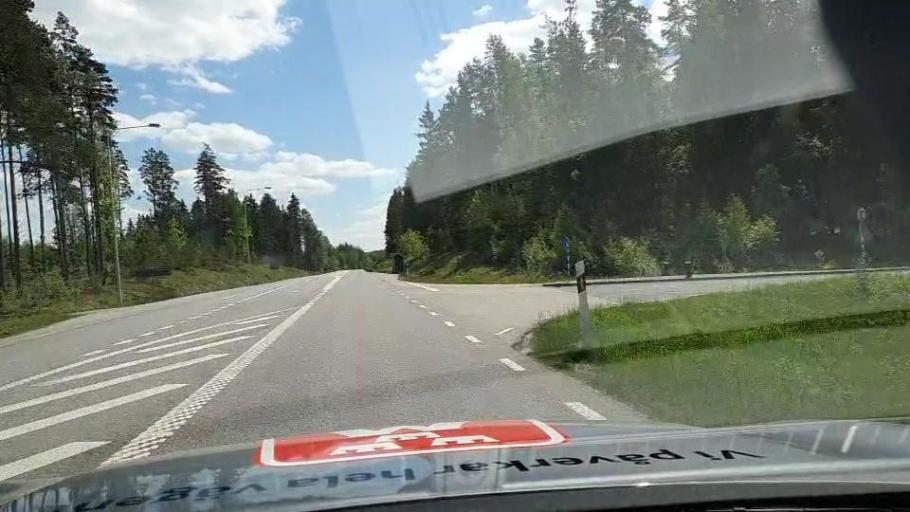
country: SE
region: Kronoberg
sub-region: Vaxjo Kommun
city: Lammhult
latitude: 57.1346
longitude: 14.6138
